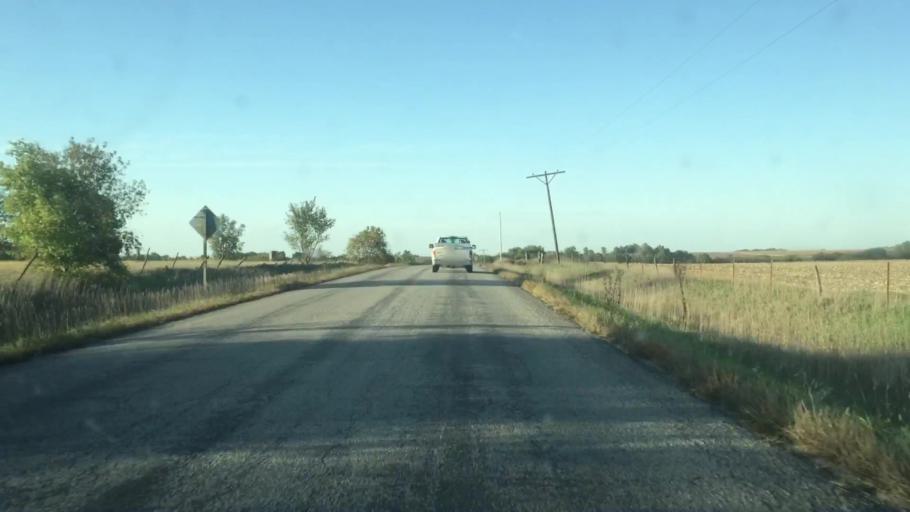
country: US
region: Kansas
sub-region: Brown County
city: Horton
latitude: 39.5523
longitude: -95.4021
